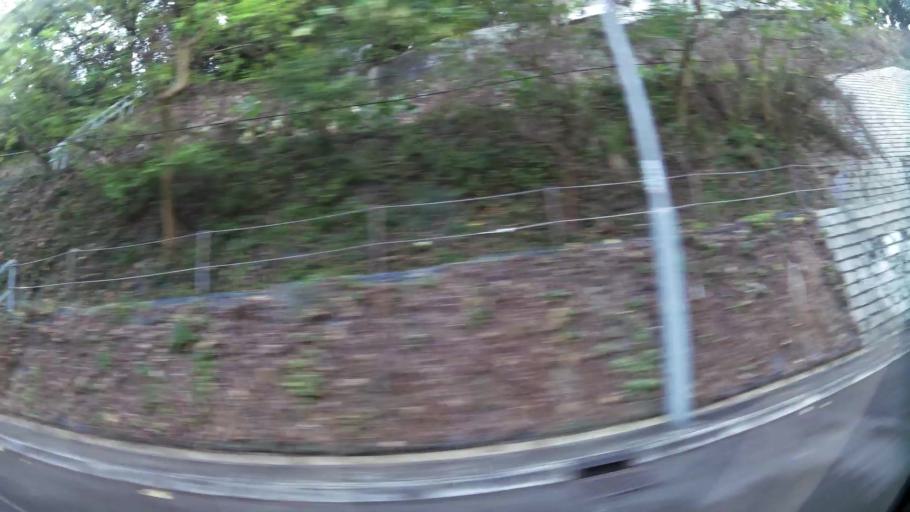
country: HK
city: Hong Kong
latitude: 22.2777
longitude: 114.1298
